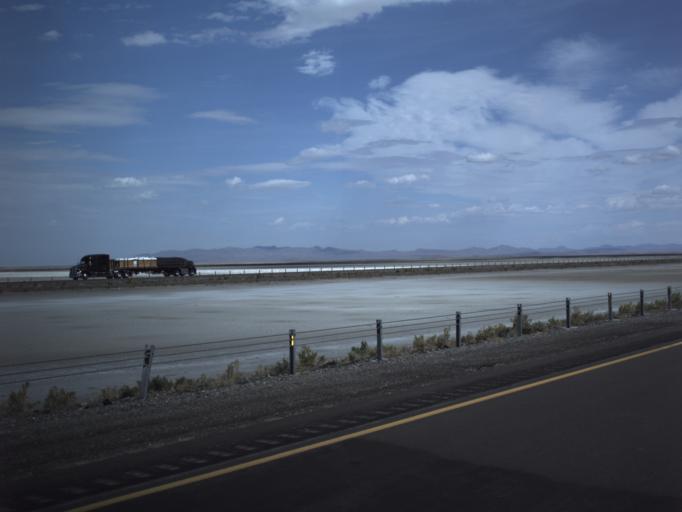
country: US
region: Utah
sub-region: Tooele County
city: Wendover
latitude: 40.7280
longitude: -113.3744
